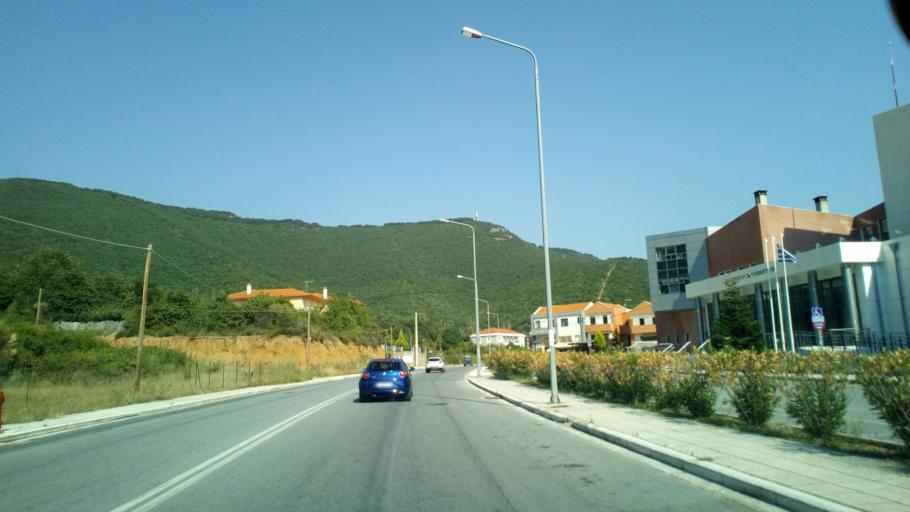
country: GR
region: Central Macedonia
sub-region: Nomos Chalkidikis
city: Polygyros
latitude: 40.3835
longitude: 23.4466
